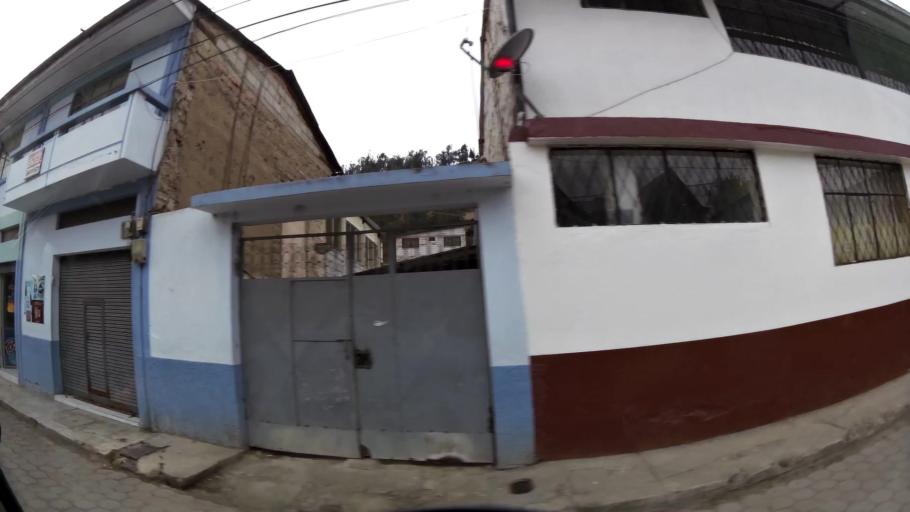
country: EC
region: Chimborazo
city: Alausi
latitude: -2.2896
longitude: -78.9190
